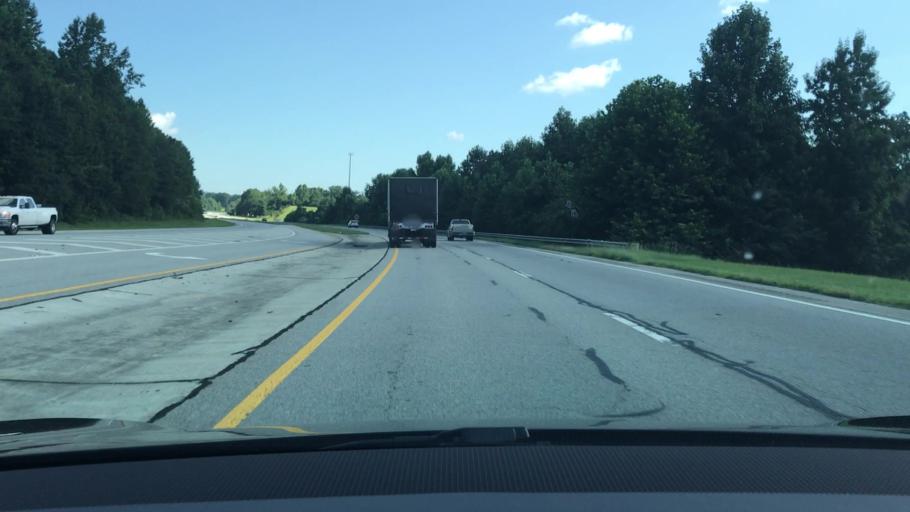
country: US
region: Georgia
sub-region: Habersham County
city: Clarkesville
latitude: 34.6789
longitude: -83.4250
